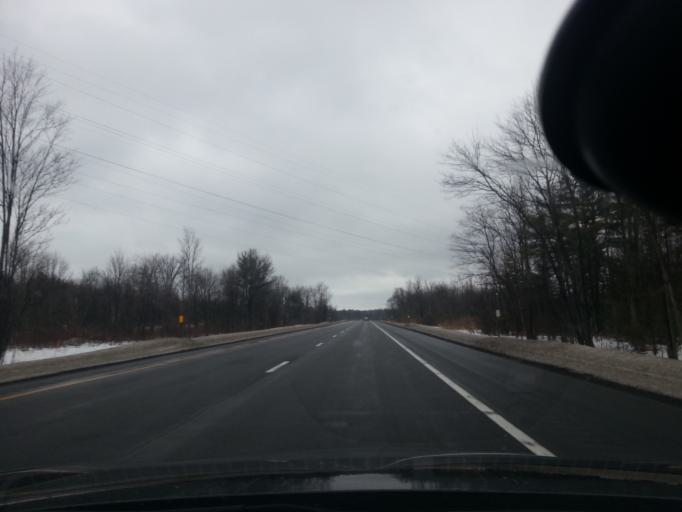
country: US
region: New York
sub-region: Oswego County
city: Central Square
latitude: 43.3413
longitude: -76.1233
